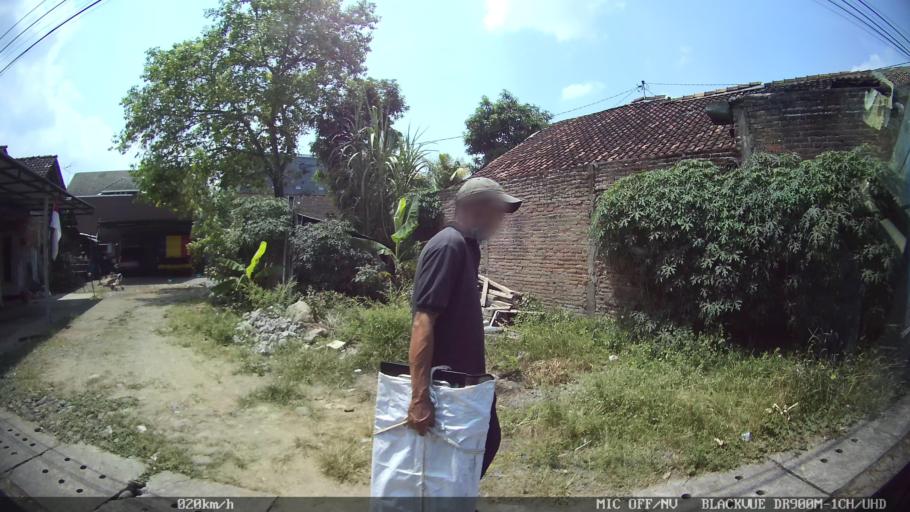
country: ID
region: Daerah Istimewa Yogyakarta
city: Yogyakarta
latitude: -7.8254
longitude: 110.4073
